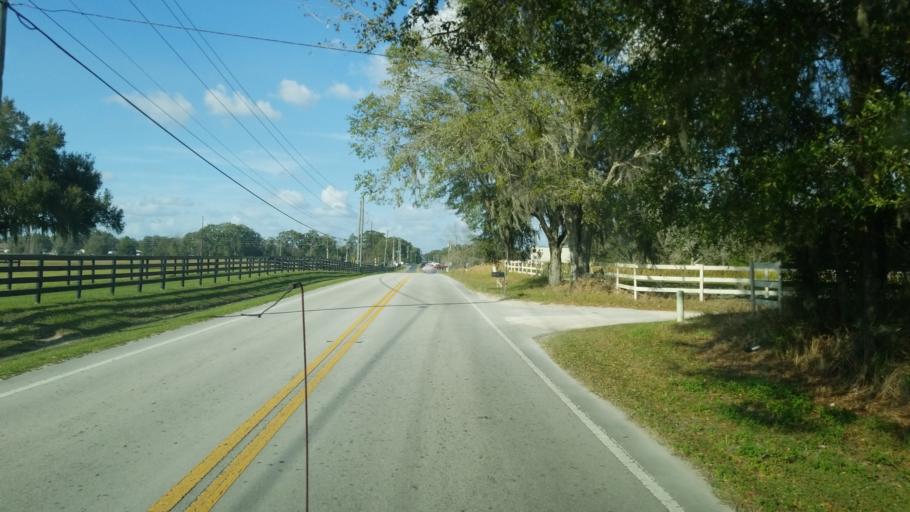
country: US
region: Florida
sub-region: Marion County
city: Ocala
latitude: 29.1834
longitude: -82.2517
